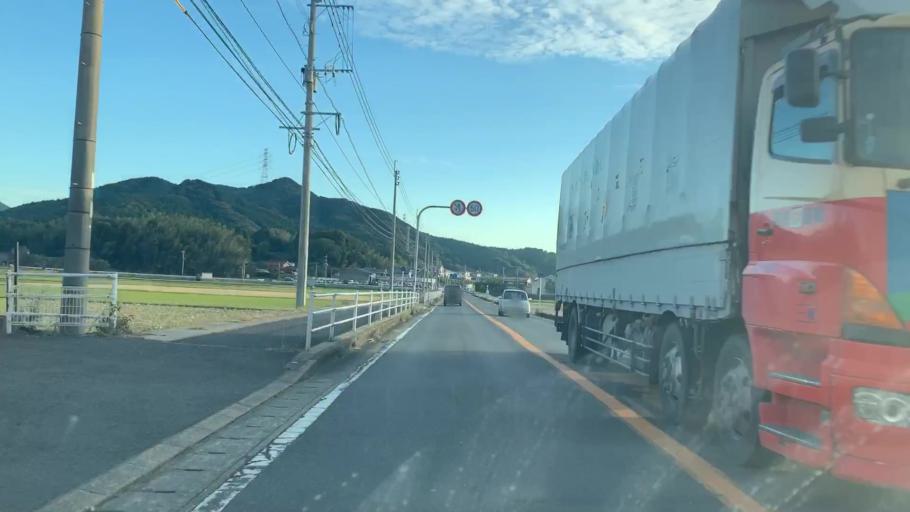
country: JP
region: Saga Prefecture
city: Karatsu
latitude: 33.4026
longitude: 129.9867
